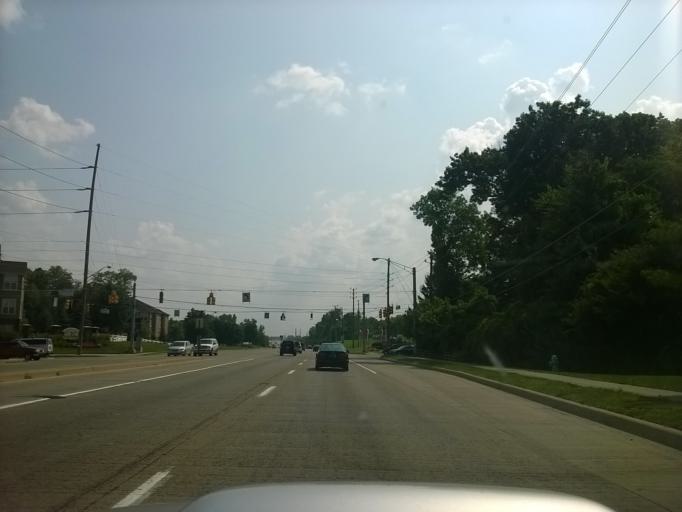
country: US
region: Indiana
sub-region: Hamilton County
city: Fishers
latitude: 39.9204
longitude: -86.0711
